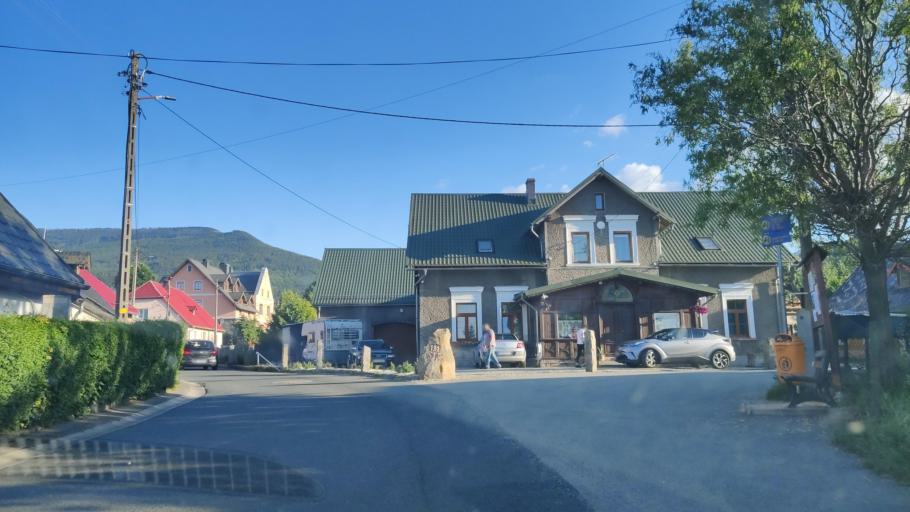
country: PL
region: Lower Silesian Voivodeship
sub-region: Powiat jeleniogorski
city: Karpacz
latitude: 50.7883
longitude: 15.7781
